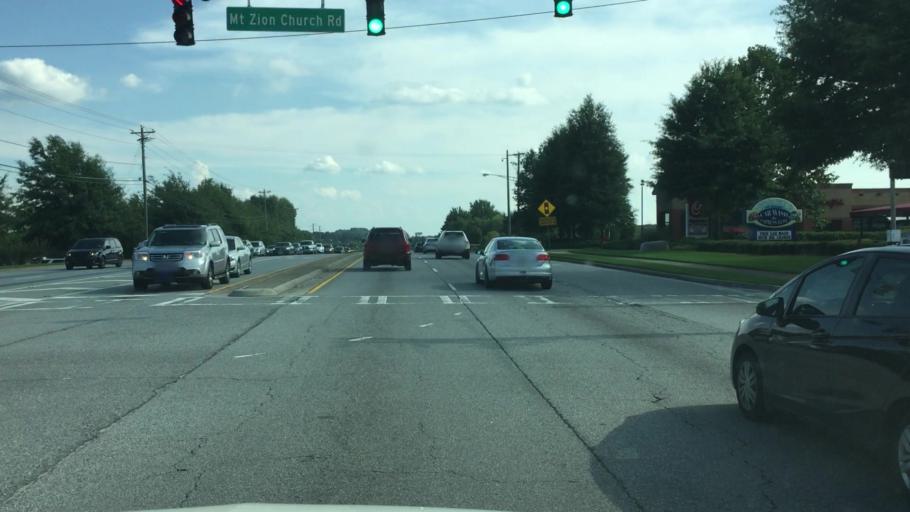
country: US
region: Georgia
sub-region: Gwinnett County
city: Snellville
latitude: 33.8883
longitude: -84.0093
